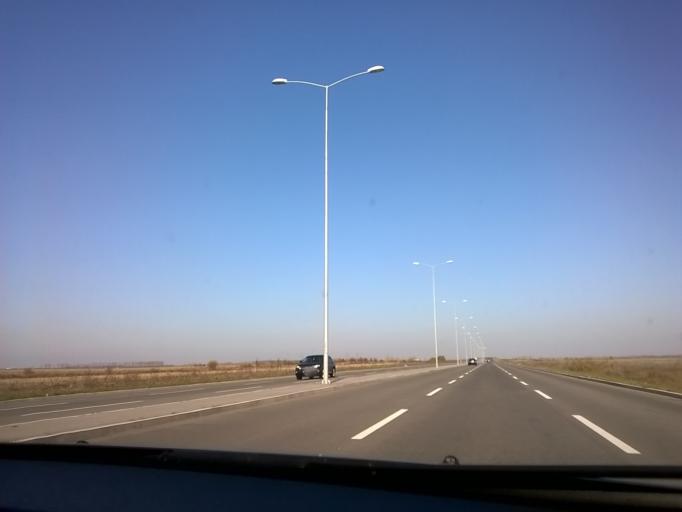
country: RS
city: Ovca
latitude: 44.9000
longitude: 20.5146
